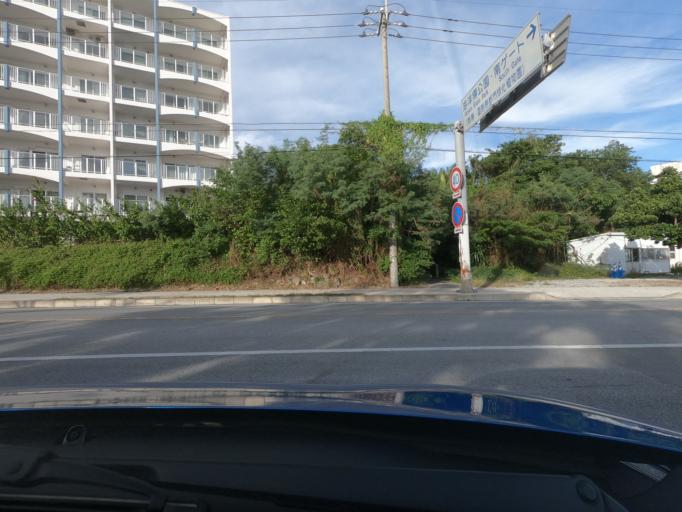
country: JP
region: Okinawa
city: Nago
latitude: 26.6814
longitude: 127.8843
